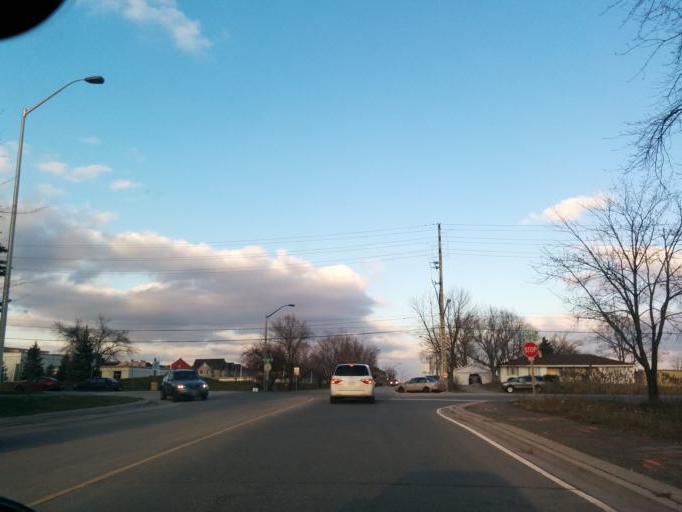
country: CA
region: Ontario
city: Burlington
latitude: 43.4328
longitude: -79.7734
